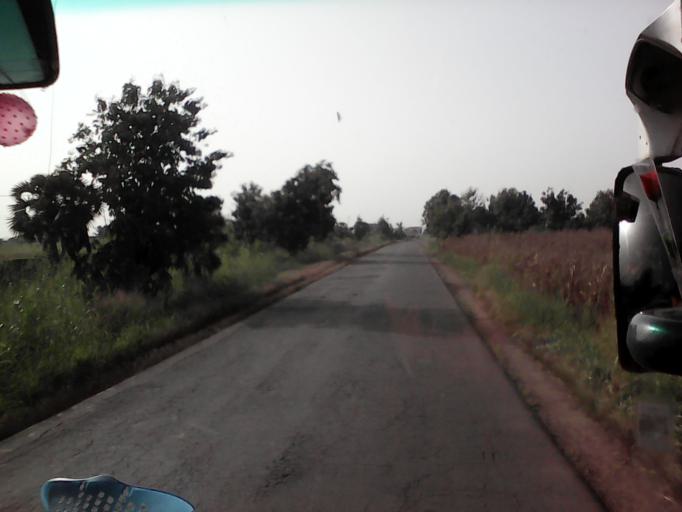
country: TG
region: Kara
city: Kara
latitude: 9.5222
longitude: 1.2080
